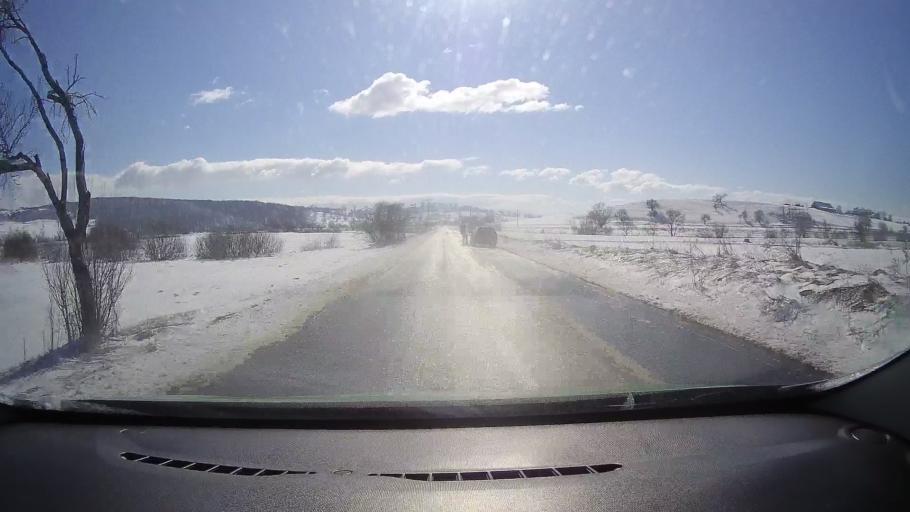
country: RO
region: Sibiu
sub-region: Comuna Vurpar
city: Vurpar
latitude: 45.8675
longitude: 24.3186
